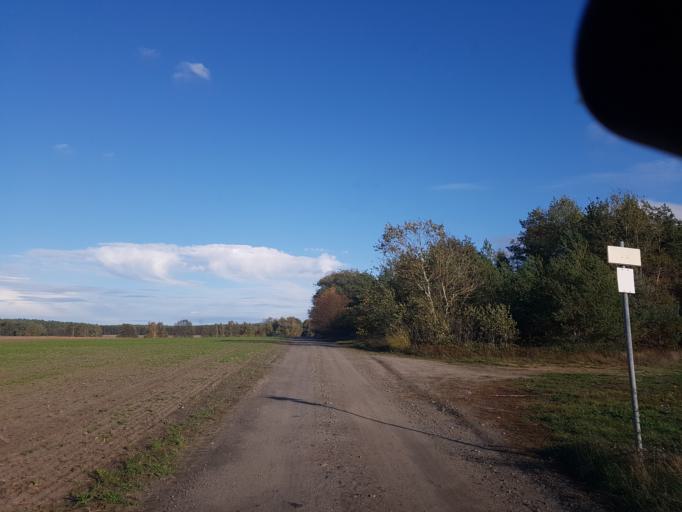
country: DE
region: Brandenburg
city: Plessa
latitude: 51.5414
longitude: 13.6740
